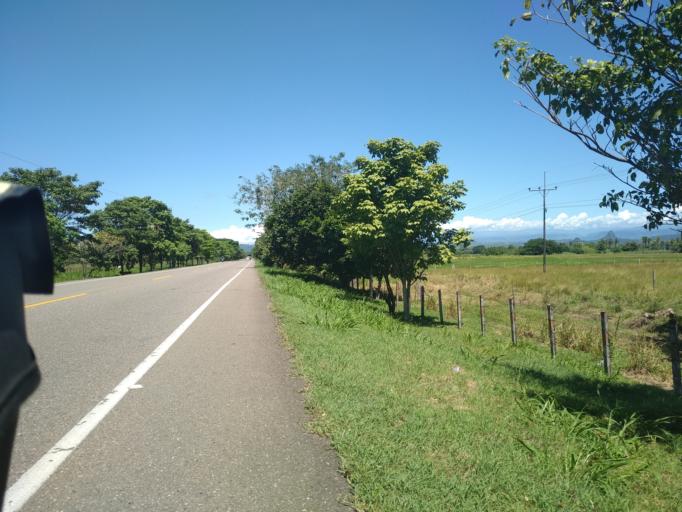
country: CO
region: Caldas
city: La Dorada
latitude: 5.3939
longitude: -74.7020
